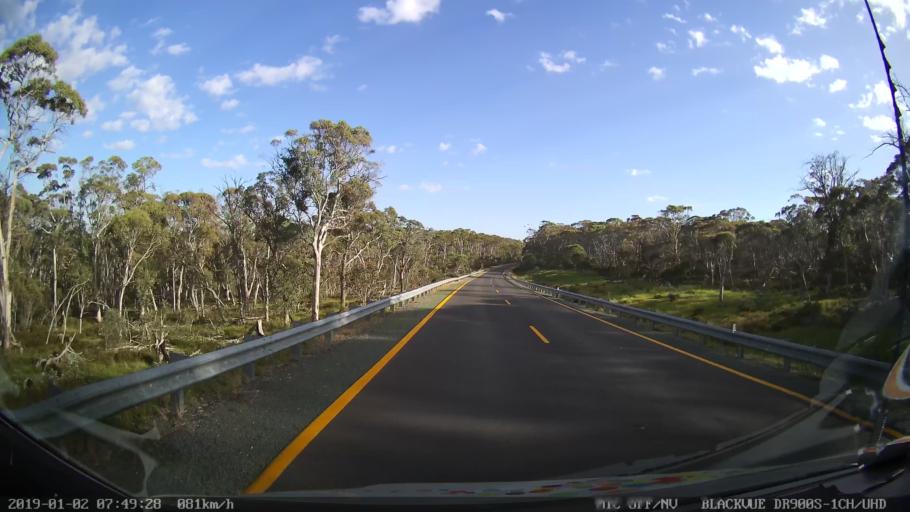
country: AU
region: New South Wales
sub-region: Tumut Shire
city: Tumut
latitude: -35.7413
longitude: 148.5224
